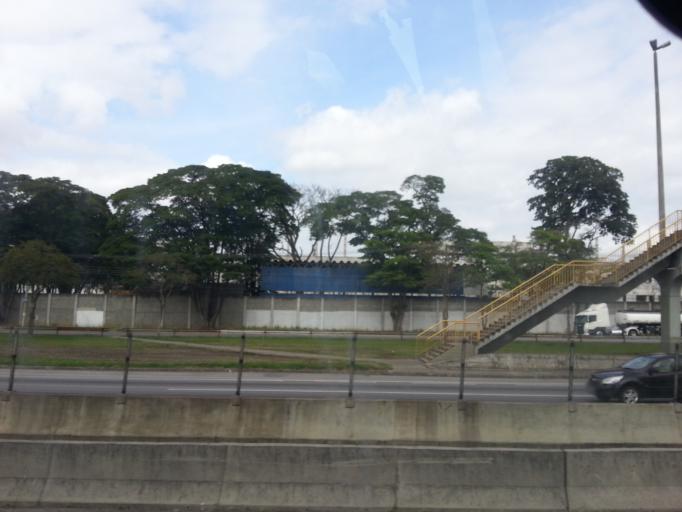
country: BR
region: Sao Paulo
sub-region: Jacarei
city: Jacarei
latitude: -23.2488
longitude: -45.9336
